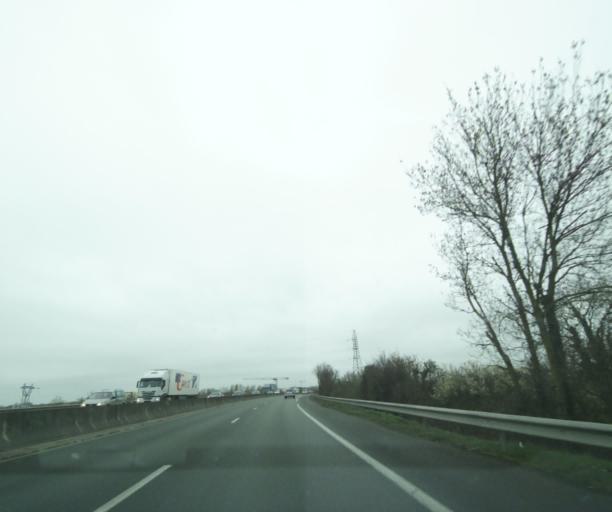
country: FR
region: Poitou-Charentes
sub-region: Departement de la Charente-Maritime
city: Perigny
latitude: 46.1602
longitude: -1.1210
